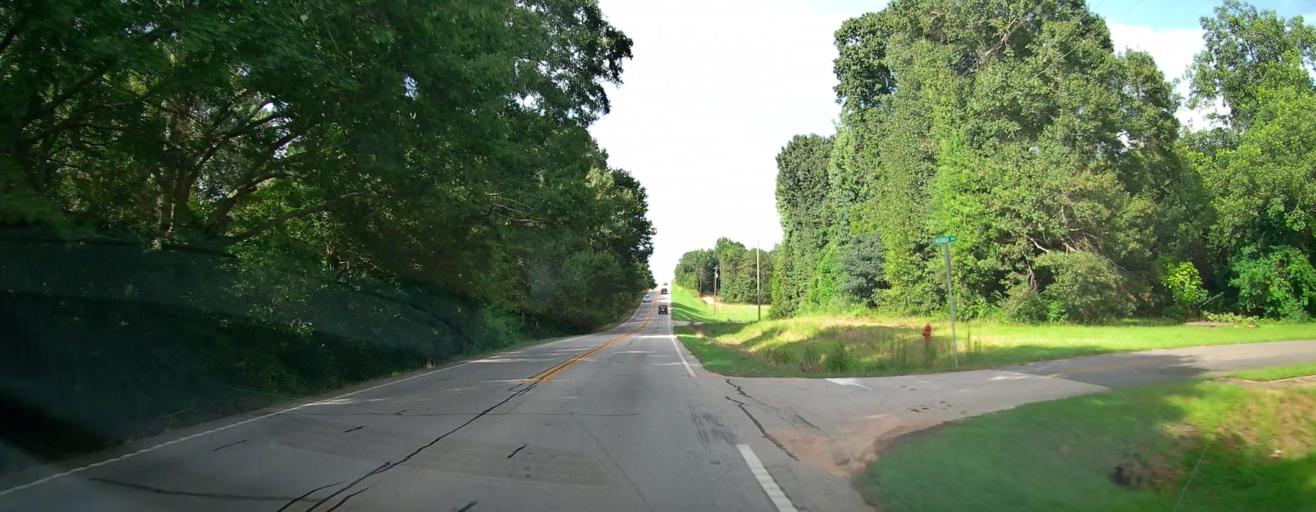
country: US
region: Georgia
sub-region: Meriwether County
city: Manchester
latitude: 32.9785
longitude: -84.5772
